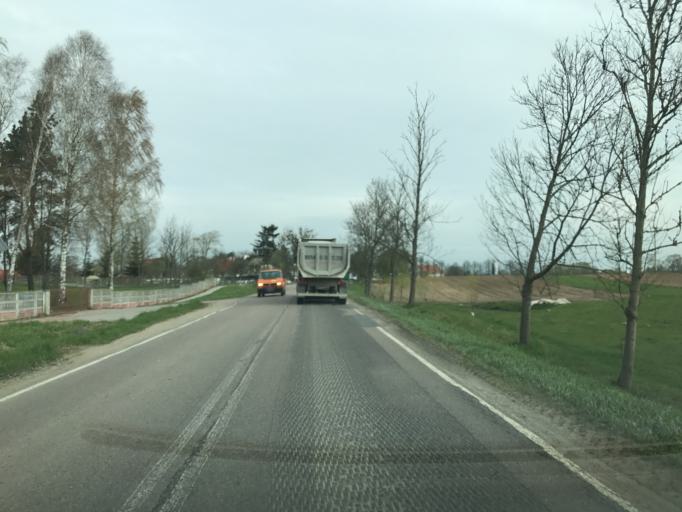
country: PL
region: Warmian-Masurian Voivodeship
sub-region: Powiat ostrodzki
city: Gierzwald
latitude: 53.5827
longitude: 20.0886
